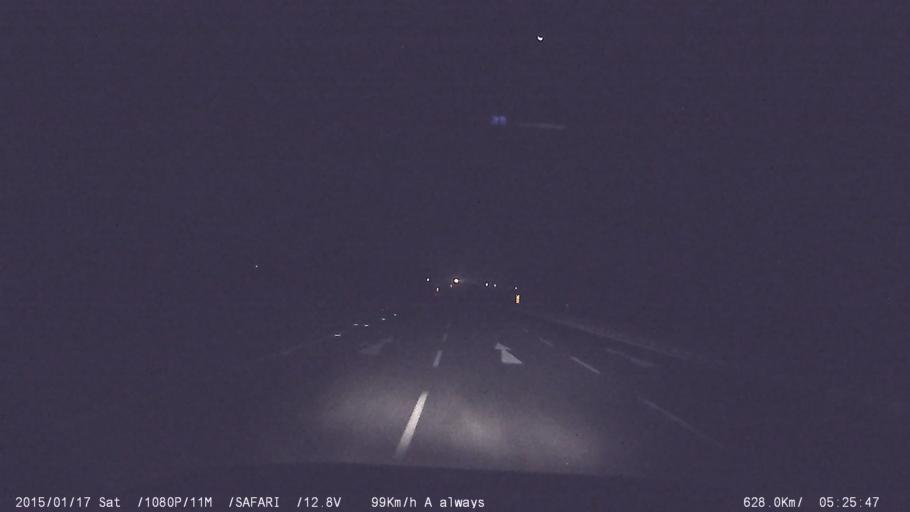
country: IN
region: Tamil Nadu
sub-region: Vellore
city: Arcot
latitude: 12.9406
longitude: 79.2376
